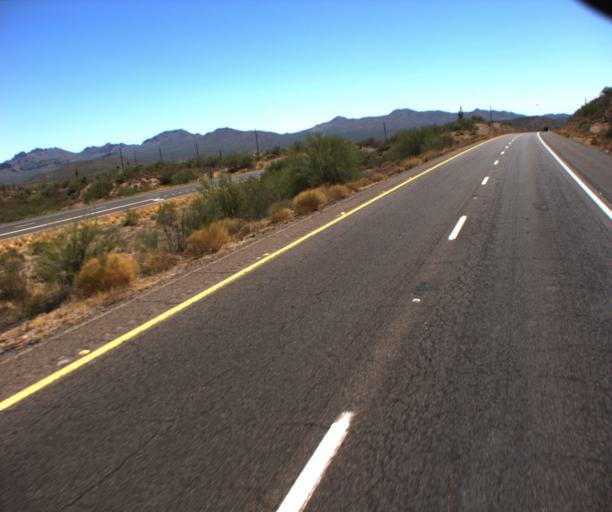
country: US
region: Arizona
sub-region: Maricopa County
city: Fountain Hills
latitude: 33.5993
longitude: -111.5891
